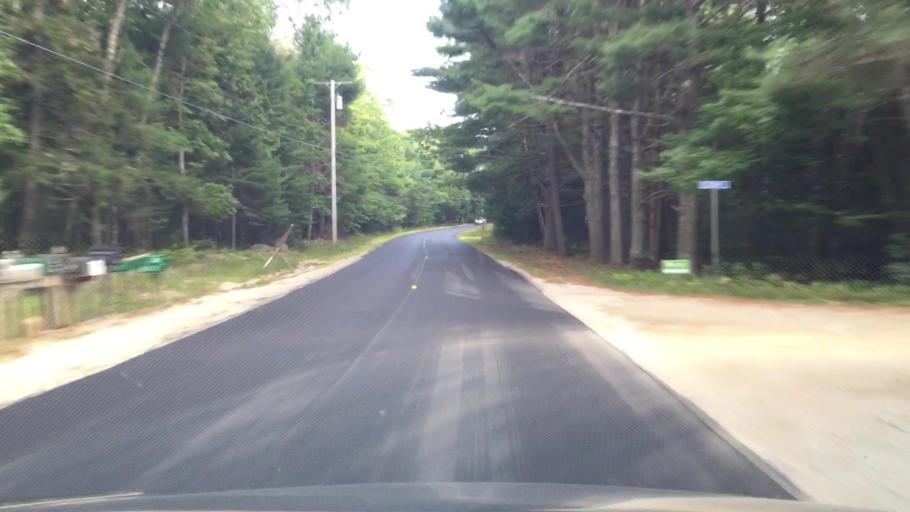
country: US
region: Maine
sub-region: Hancock County
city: Surry
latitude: 44.5235
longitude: -68.6089
